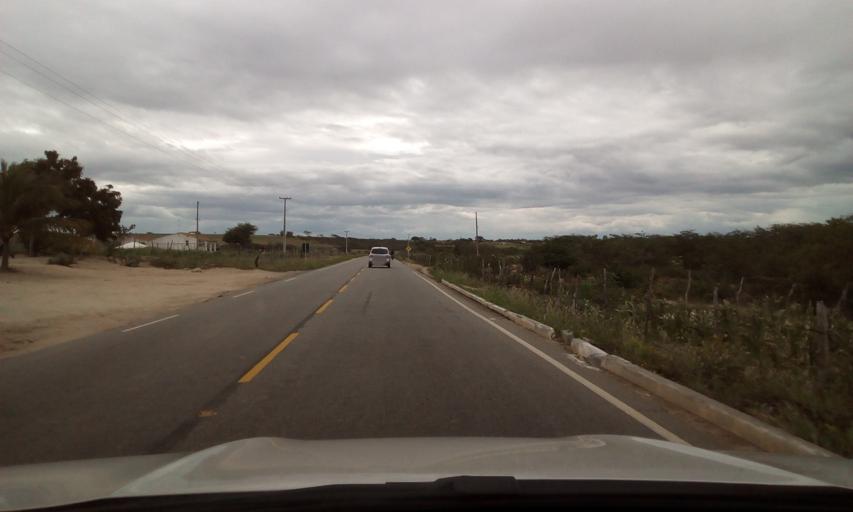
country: BR
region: Paraiba
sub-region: Picui
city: Picui
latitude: -6.5584
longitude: -36.2903
